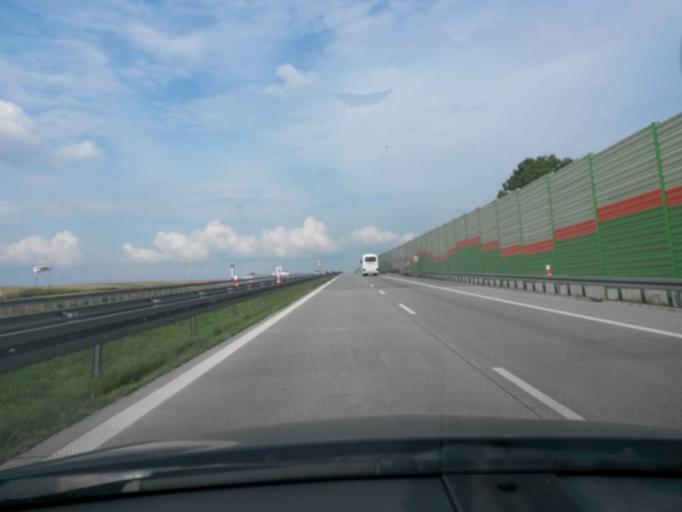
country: PL
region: Lodz Voivodeship
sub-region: Powiat tomaszowski
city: Tomaszow Mazowiecki
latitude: 51.5379
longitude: 19.9606
